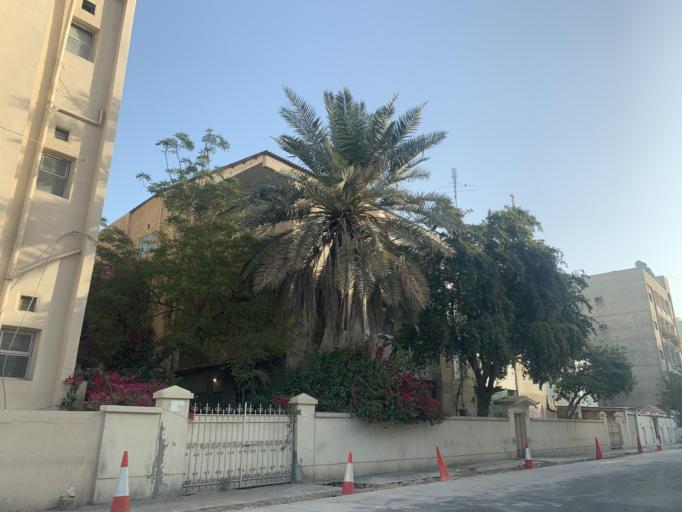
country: BH
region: Manama
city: Manama
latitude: 26.2157
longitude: 50.5857
